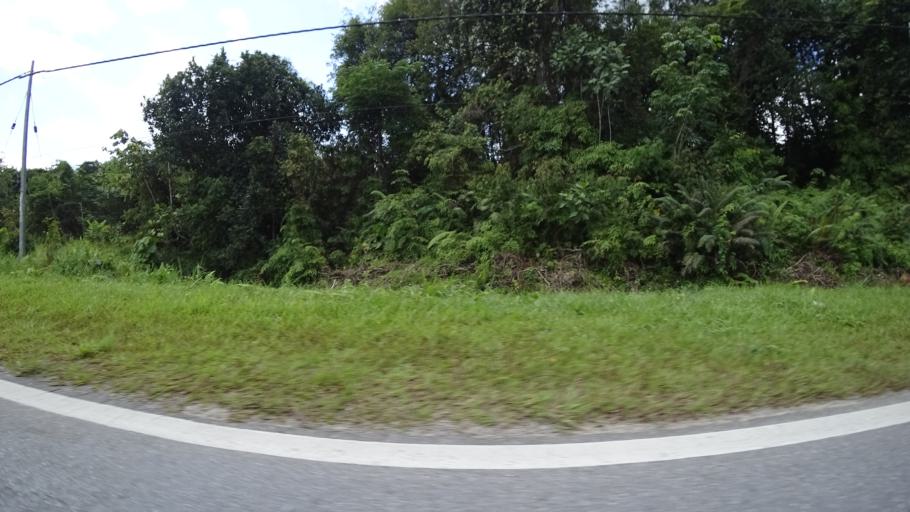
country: MY
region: Sarawak
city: Limbang
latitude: 4.6556
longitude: 114.9579
